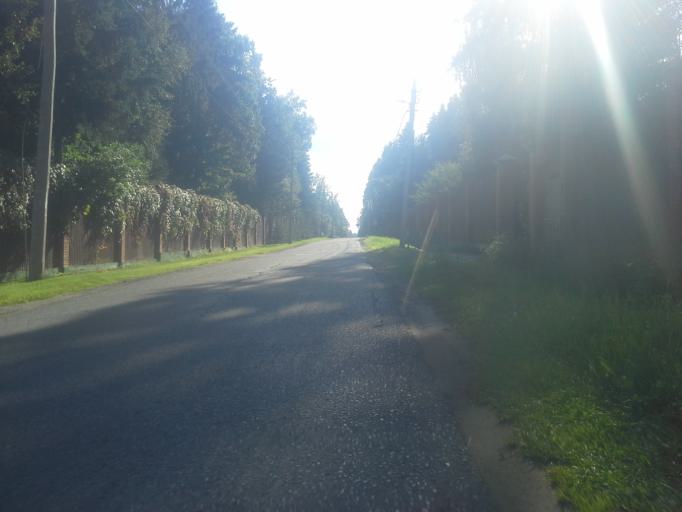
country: RU
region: Moskovskaya
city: Selyatino
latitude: 55.4736
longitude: 37.0100
